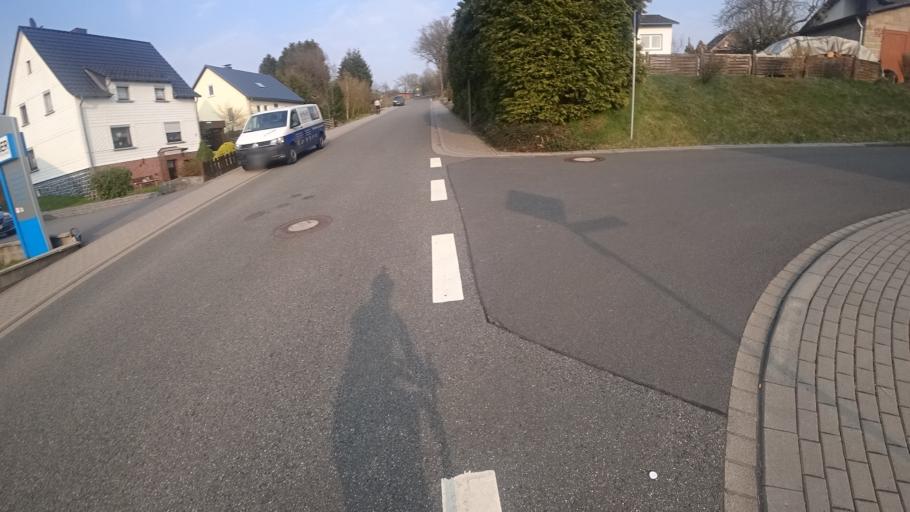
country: DE
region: Rheinland-Pfalz
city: Luckenbach
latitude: 50.7040
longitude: 7.8369
